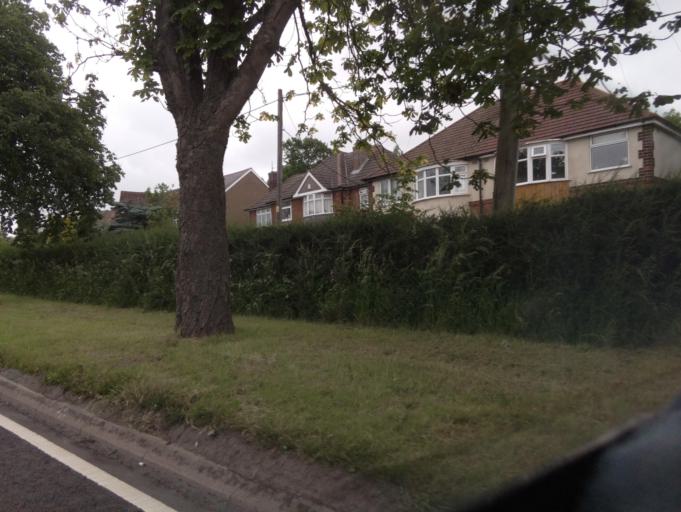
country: GB
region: England
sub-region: Leicestershire
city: Markfield
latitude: 52.6831
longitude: -1.2637
